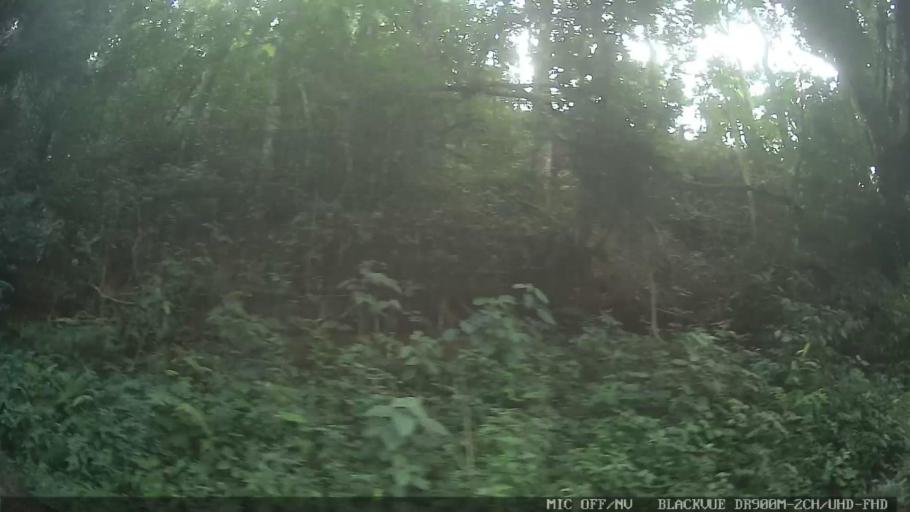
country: BR
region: Minas Gerais
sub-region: Extrema
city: Extrema
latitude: -22.8269
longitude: -46.2403
